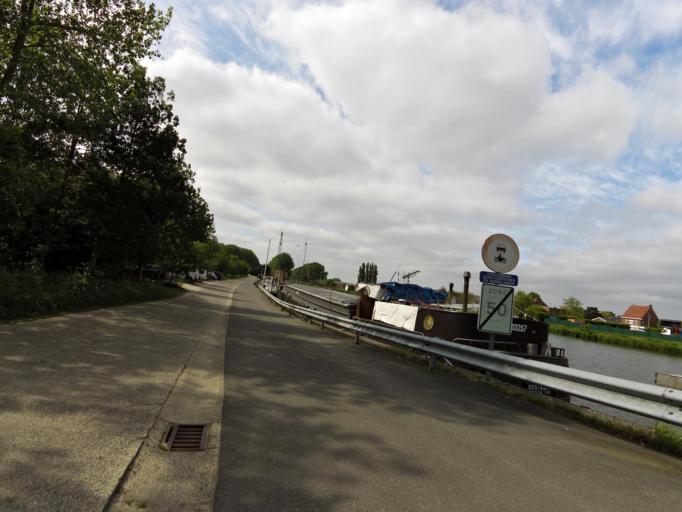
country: BE
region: Flanders
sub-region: Provincie West-Vlaanderen
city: Oostkamp
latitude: 51.1597
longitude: 3.2600
